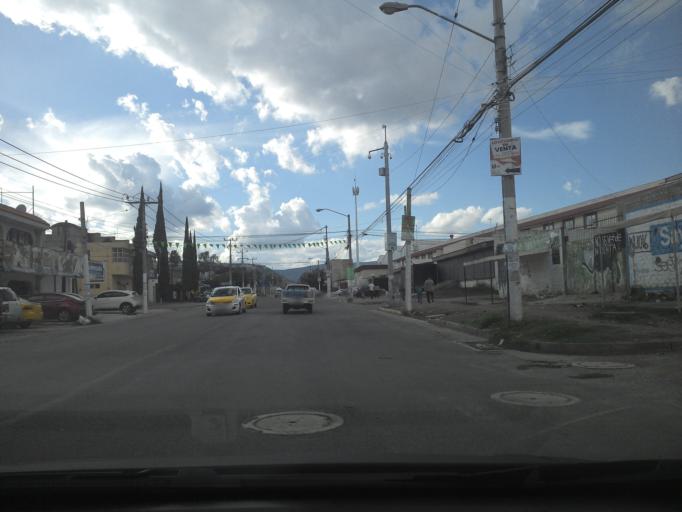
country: MX
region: Jalisco
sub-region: Tlajomulco de Zuniga
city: Palomar
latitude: 20.6147
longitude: -103.4379
